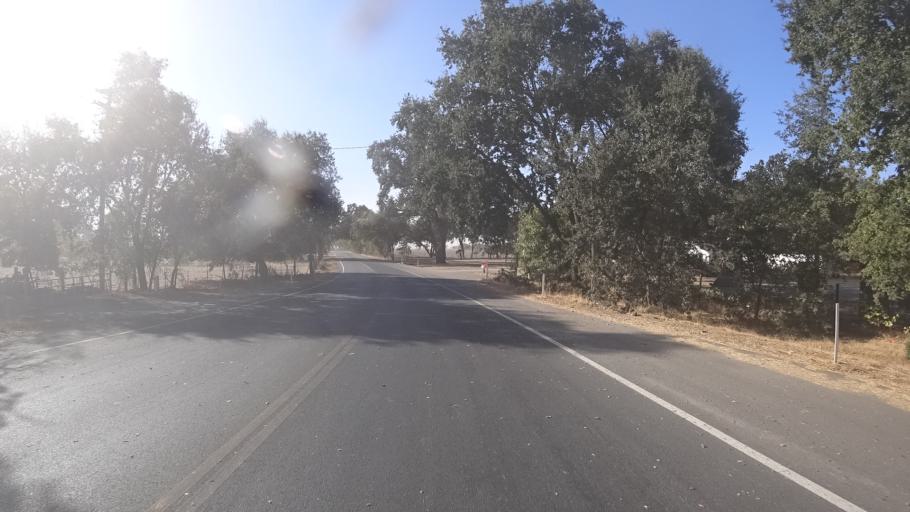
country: US
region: California
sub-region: Yolo County
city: Woodland
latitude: 38.7924
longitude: -121.7279
